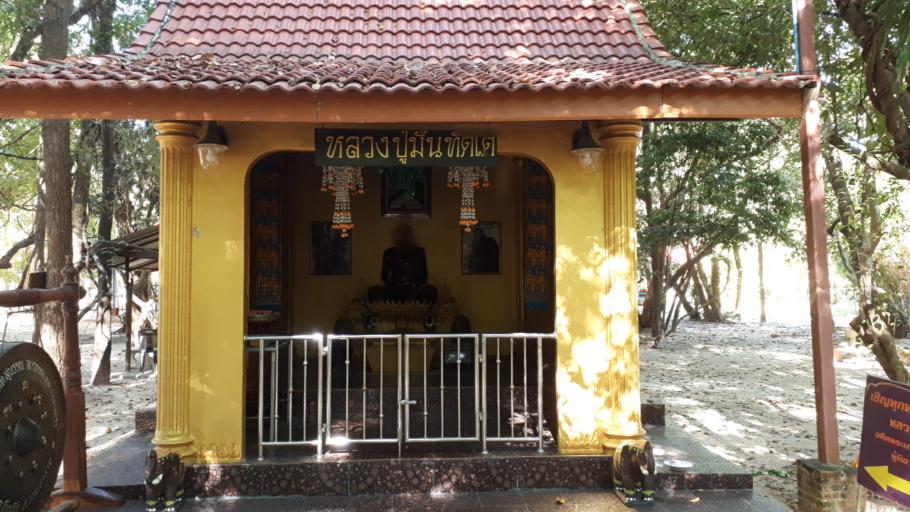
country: TH
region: Changwat Ubon Ratchathani
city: Warin Chamrap
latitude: 15.1348
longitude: 104.8462
